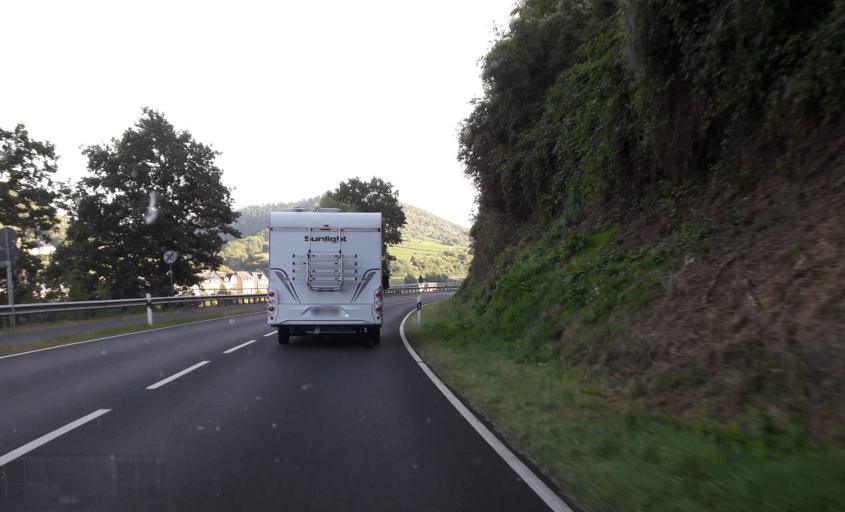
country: DE
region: Rheinland-Pfalz
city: Neef
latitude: 50.0939
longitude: 7.1351
